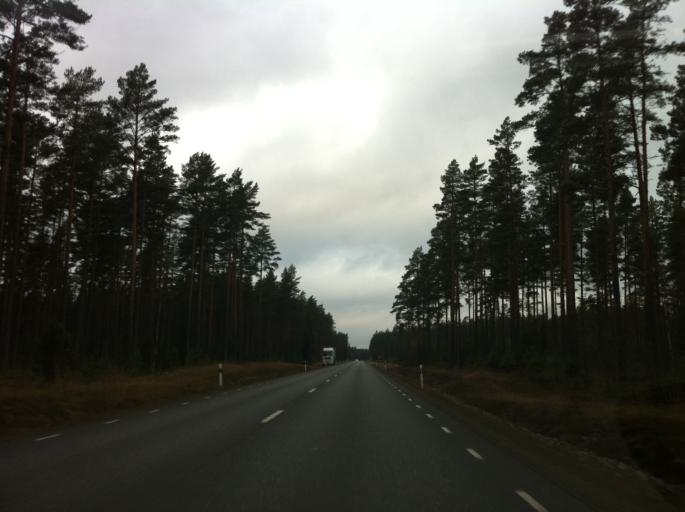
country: SE
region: Joenkoeping
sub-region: Vetlanda Kommun
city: Vetlanda
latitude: 57.4081
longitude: 15.2915
